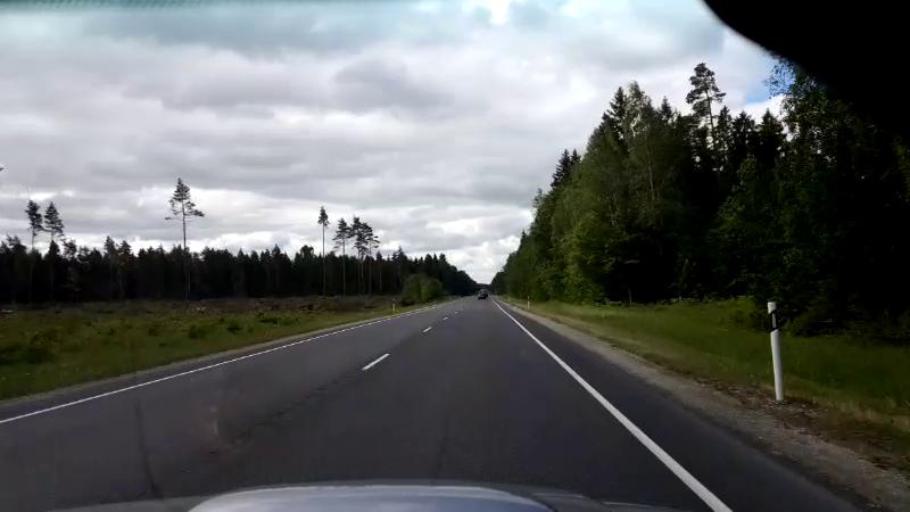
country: EE
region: Raplamaa
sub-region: Maerjamaa vald
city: Marjamaa
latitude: 58.9085
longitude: 24.4561
